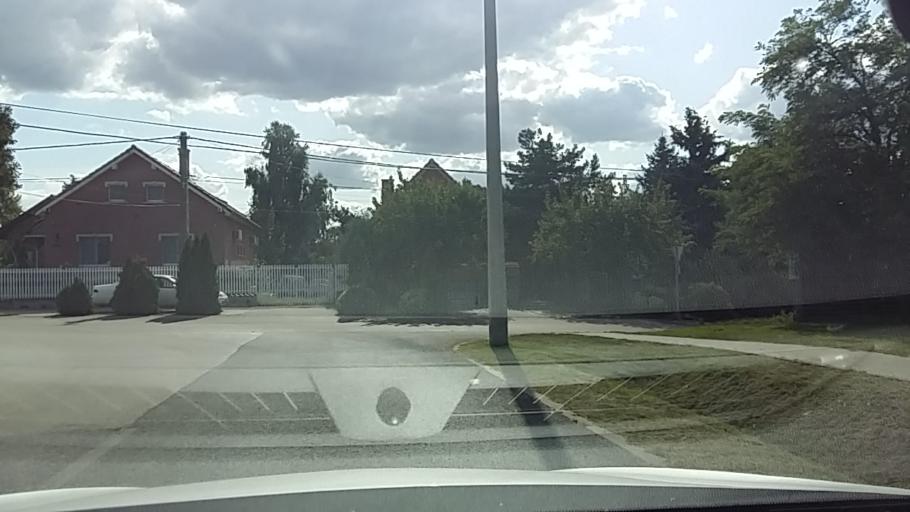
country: HU
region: Pest
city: Vecses
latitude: 47.4138
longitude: 19.2517
